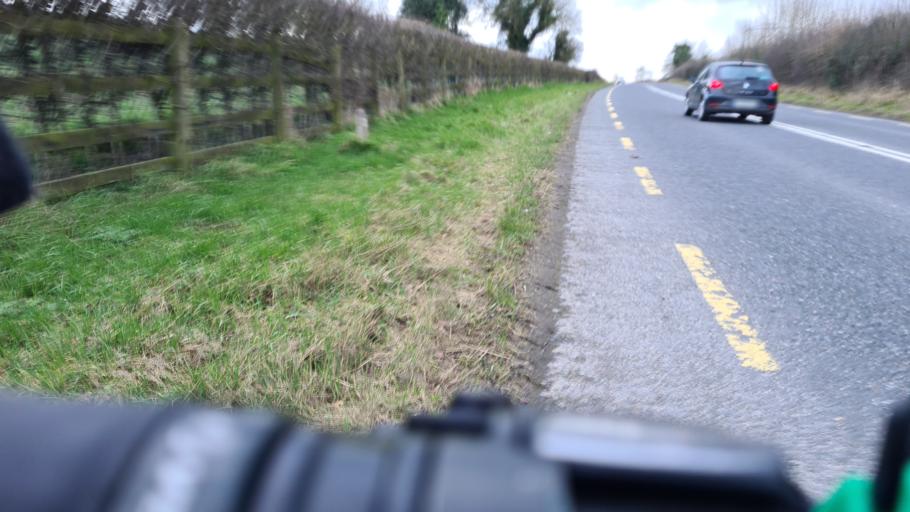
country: IE
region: Leinster
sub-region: Kildare
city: Maynooth
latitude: 53.3480
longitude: -6.6002
